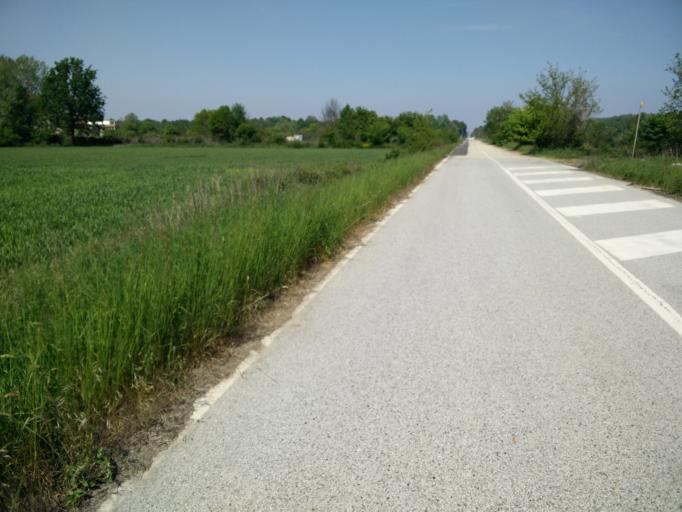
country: IT
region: Piedmont
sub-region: Provincia di Torino
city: Candiolo
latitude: 44.9615
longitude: 7.5669
